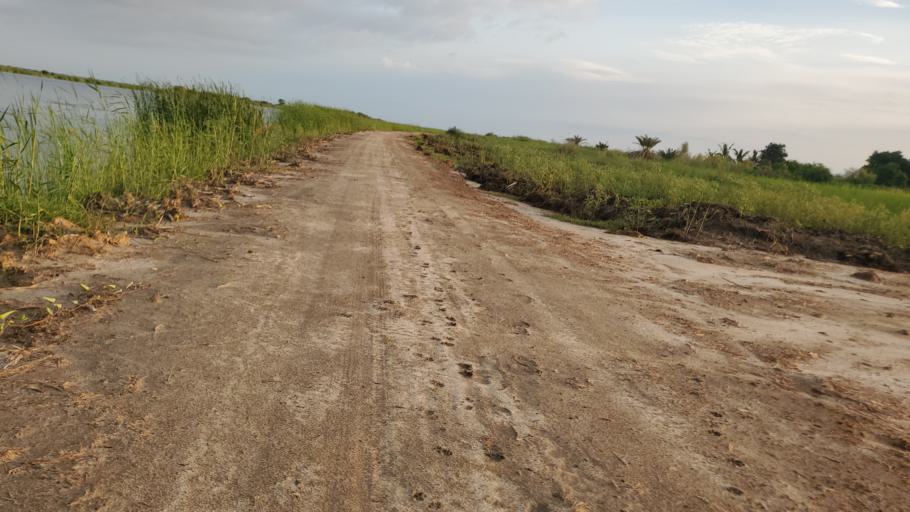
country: SN
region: Saint-Louis
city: Saint-Louis
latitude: 16.0144
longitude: -16.4005
